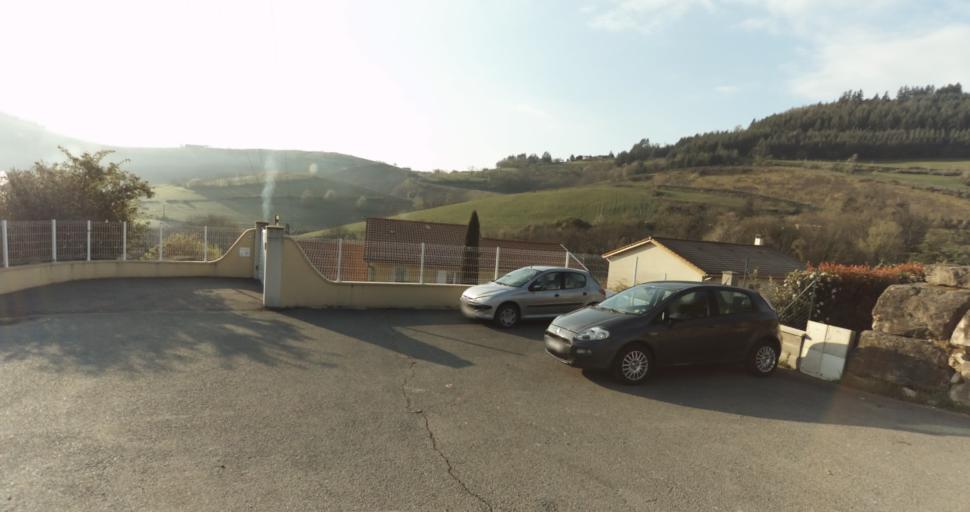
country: FR
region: Rhone-Alpes
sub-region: Departement du Rhone
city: Tarare
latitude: 45.8845
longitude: 4.4317
